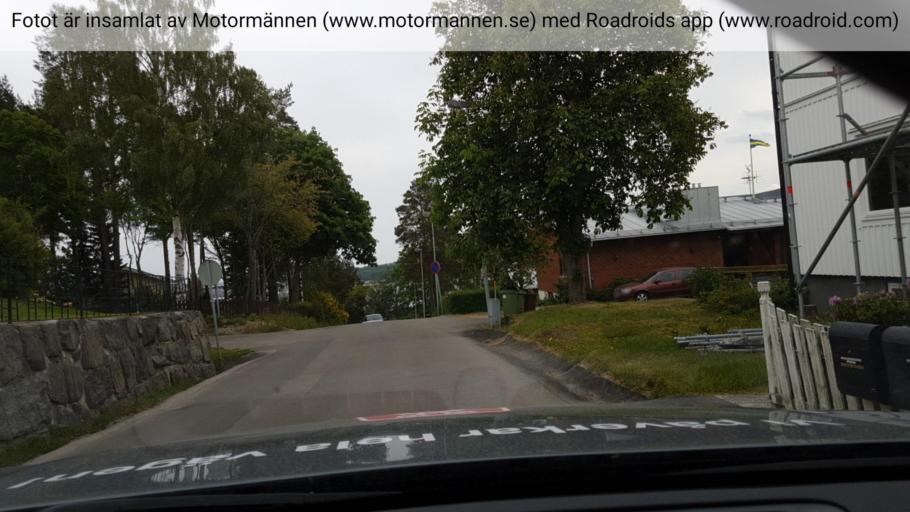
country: SE
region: Vaesternorrland
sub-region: Sundsvalls Kommun
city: Sundsvall
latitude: 62.3975
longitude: 17.3224
